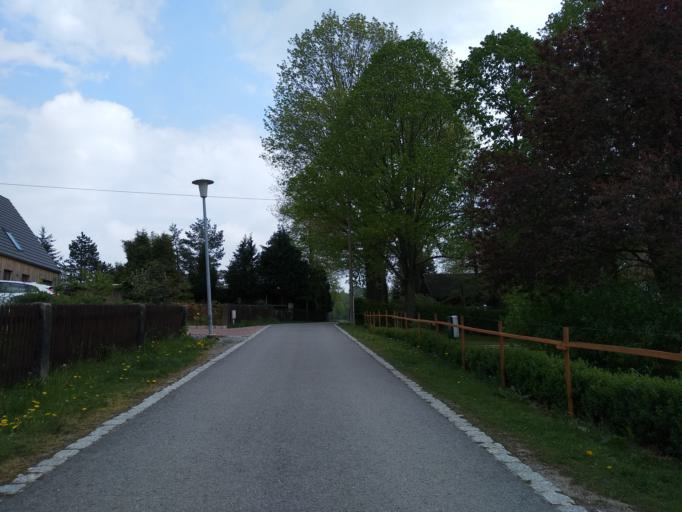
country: DE
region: Saxony
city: Porschdorf
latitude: 50.9560
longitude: 14.1380
